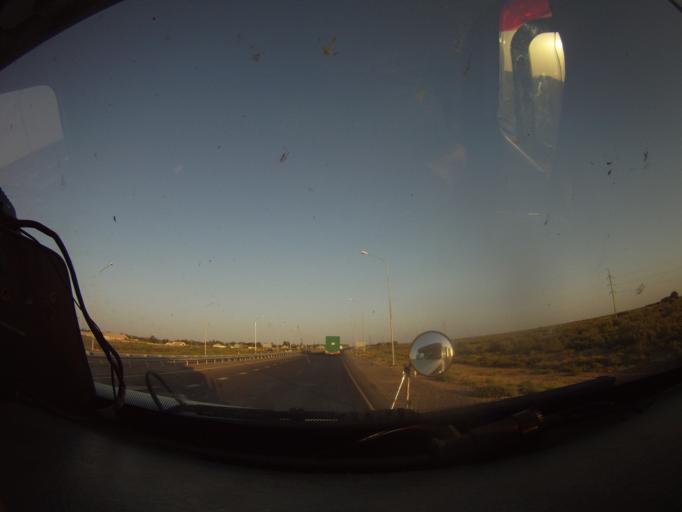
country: KZ
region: Qyzylorda
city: Shieli
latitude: 44.1420
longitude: 66.9607
